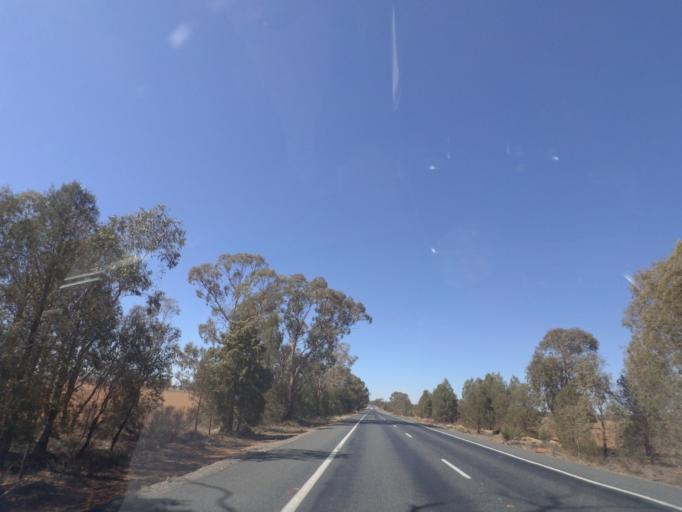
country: AU
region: New South Wales
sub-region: Bland
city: West Wyalong
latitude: -34.1845
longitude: 147.1128
